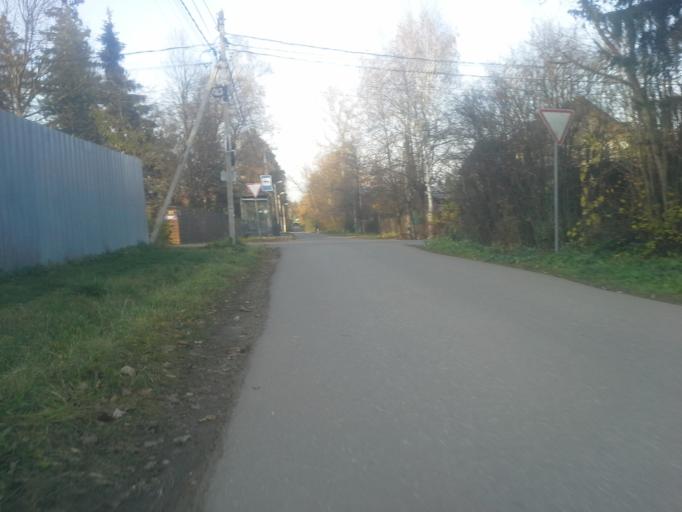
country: RU
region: Moskovskaya
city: Golitsyno
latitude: 55.6056
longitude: 36.9946
